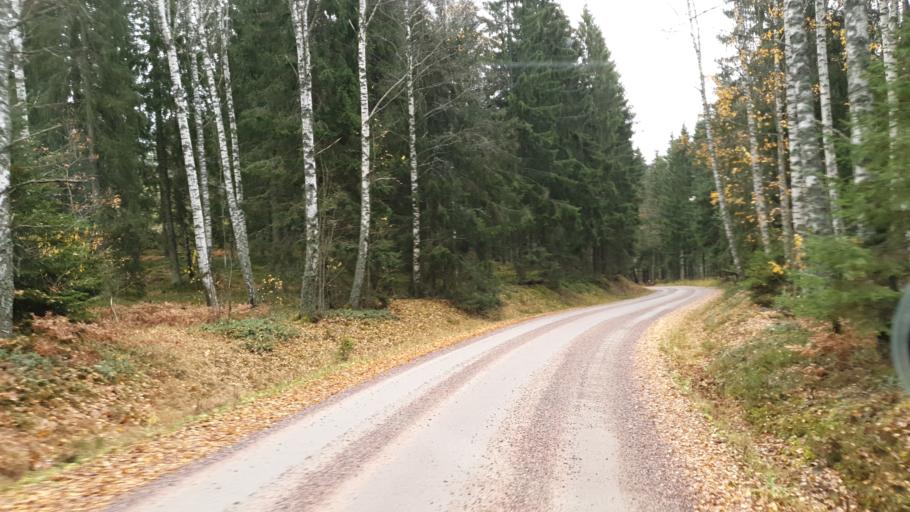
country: FI
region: Uusimaa
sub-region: Helsinki
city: Siuntio
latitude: 60.1387
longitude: 24.2707
